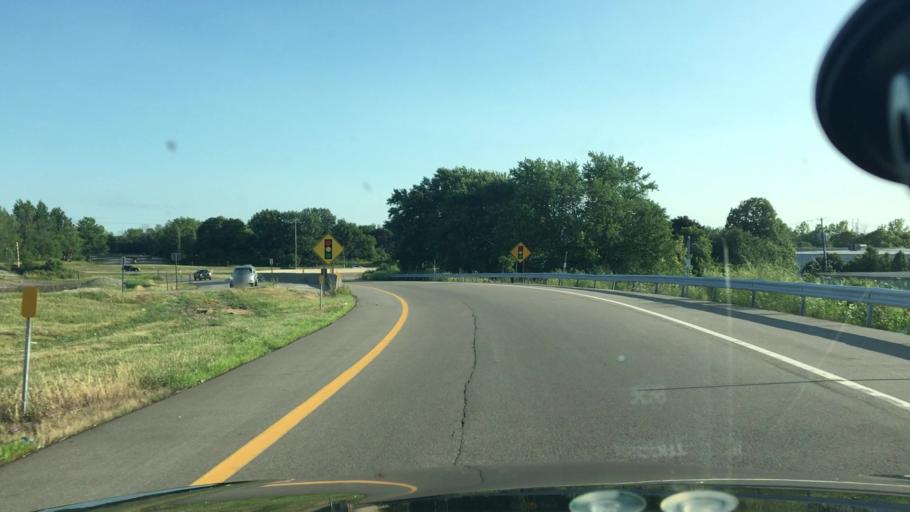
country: US
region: New York
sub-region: Erie County
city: Orchard Park
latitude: 42.7914
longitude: -78.7772
